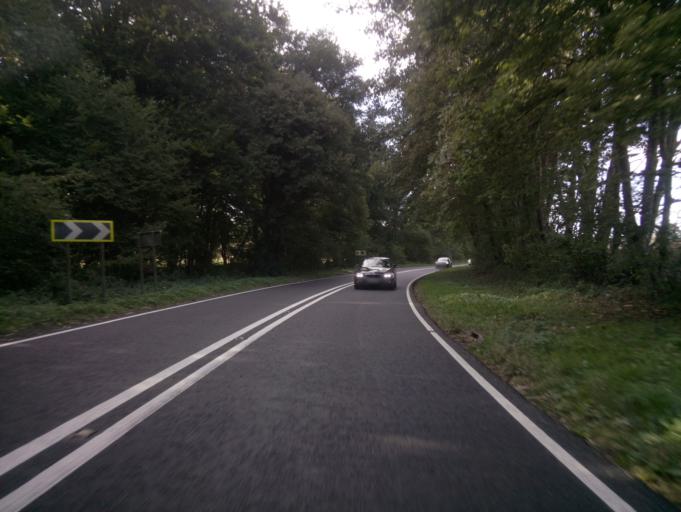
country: GB
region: England
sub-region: Hampshire
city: Four Marks
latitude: 51.1751
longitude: -1.0541
